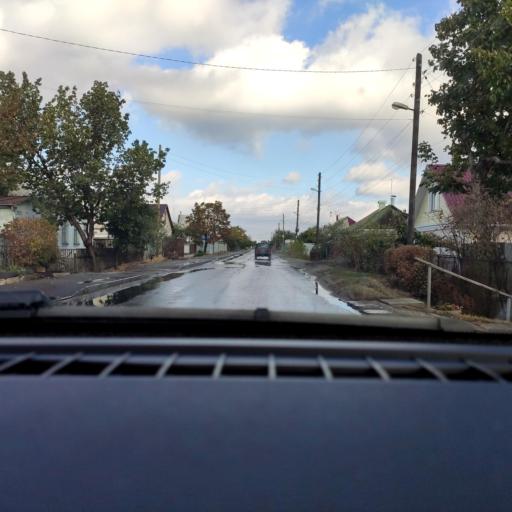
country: RU
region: Voronezj
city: Maslovka
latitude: 51.6074
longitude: 39.2207
